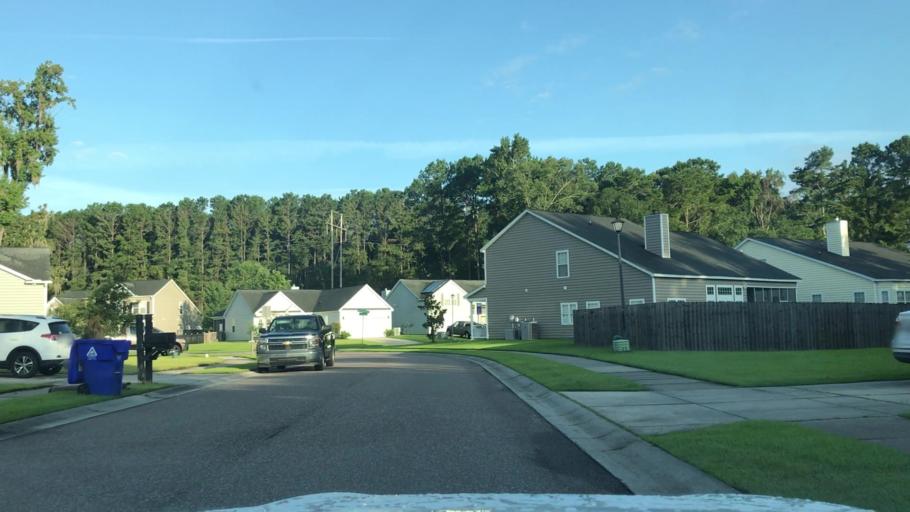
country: US
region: South Carolina
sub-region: Charleston County
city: Shell Point
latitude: 32.8380
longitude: -80.1001
